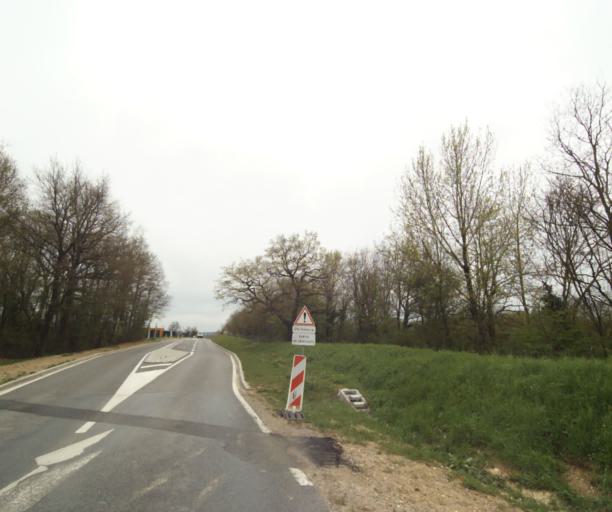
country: FR
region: Bourgogne
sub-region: Departement de Saone-et-Loire
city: Charnay-les-Macon
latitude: 46.2942
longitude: 4.7920
